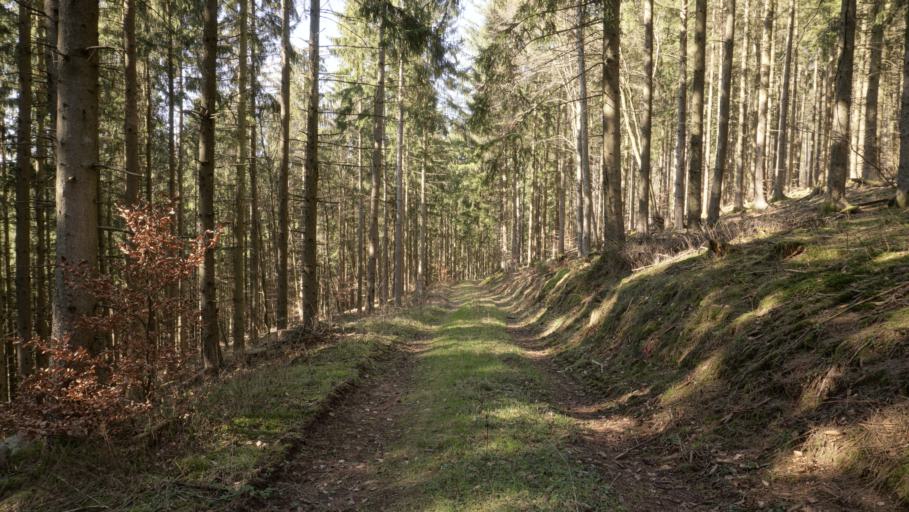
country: DE
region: Baden-Wuerttemberg
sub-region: Karlsruhe Region
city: Neckargerach
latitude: 49.4238
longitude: 9.1003
